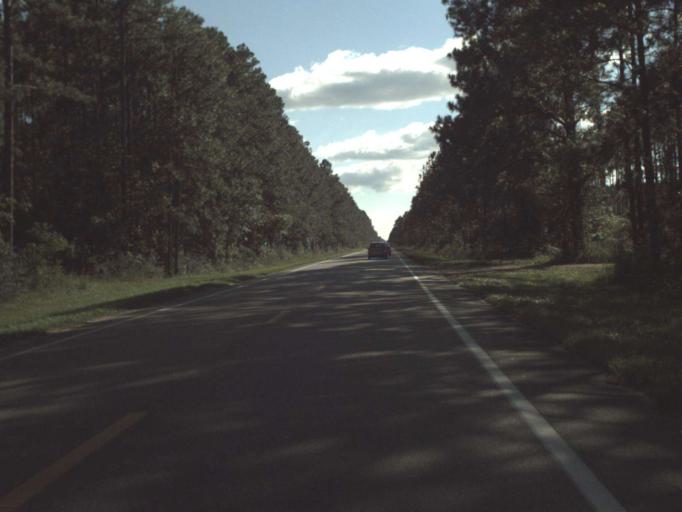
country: US
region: Florida
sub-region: Gulf County
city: Port Saint Joe
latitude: 29.9349
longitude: -85.1908
